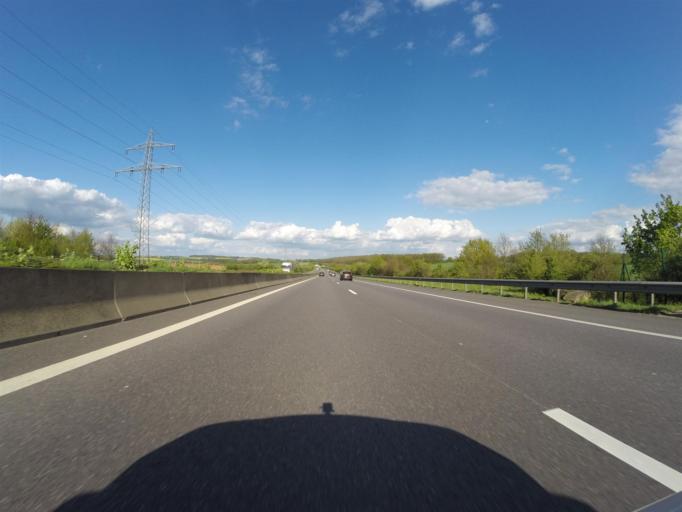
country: LU
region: Luxembourg
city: Aspelt
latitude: 49.5101
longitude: 6.2119
